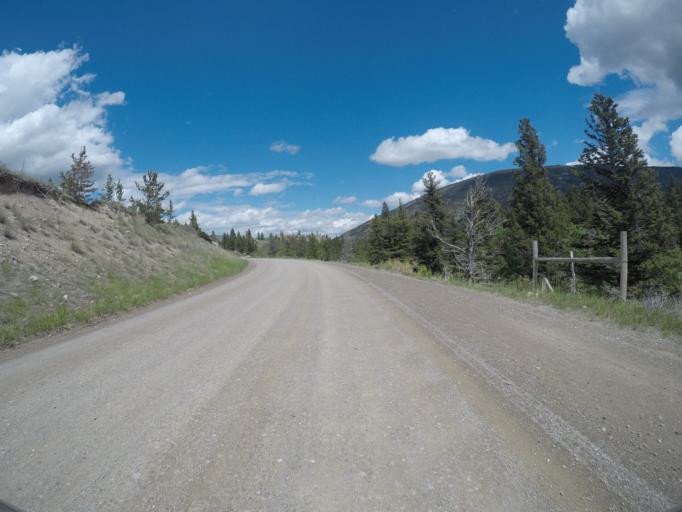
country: US
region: Montana
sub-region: Park County
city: Livingston
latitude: 45.5478
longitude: -110.2113
